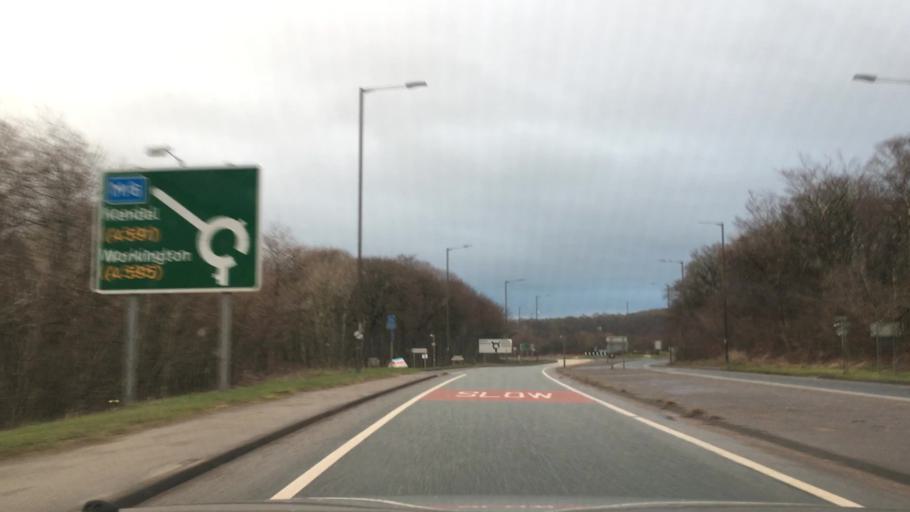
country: GB
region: England
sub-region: Cumbria
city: Askam in Furness
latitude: 54.1562
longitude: -3.2138
